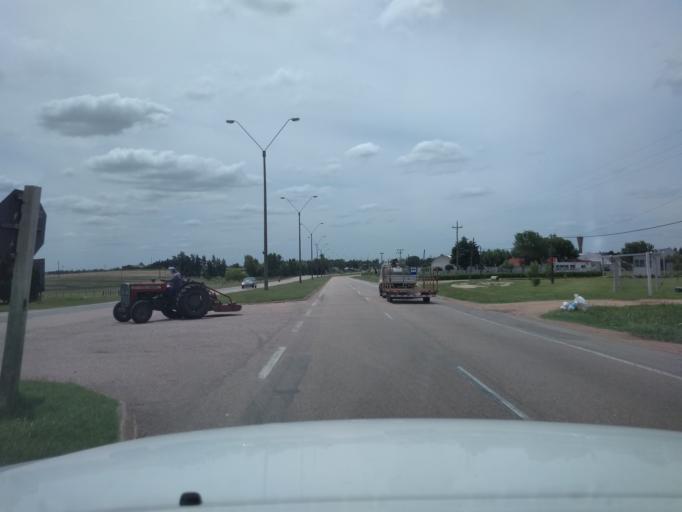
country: UY
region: Canelones
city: Joanico
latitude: -34.6017
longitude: -56.2611
